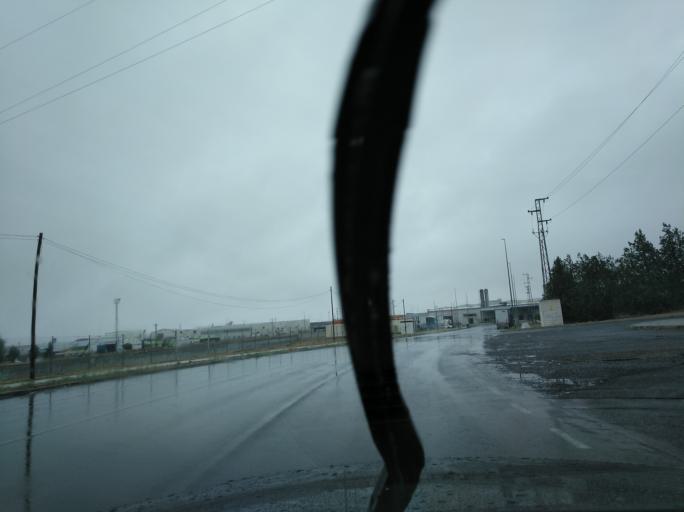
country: ES
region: Extremadura
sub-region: Provincia de Badajoz
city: Badajoz
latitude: 38.8948
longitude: -6.9858
